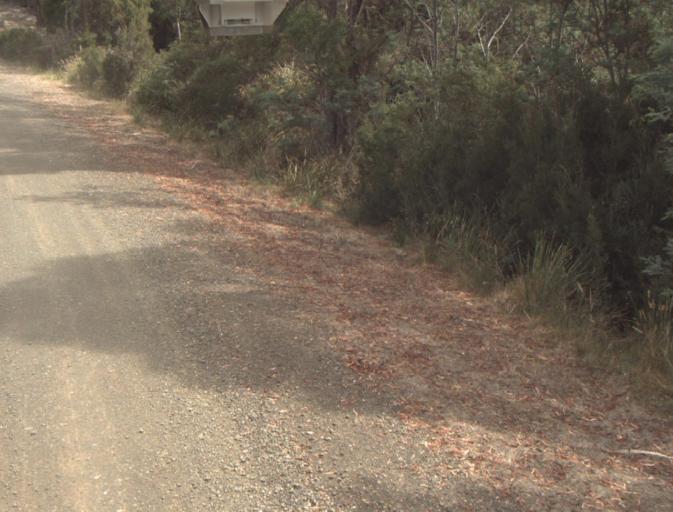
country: AU
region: Tasmania
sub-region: Launceston
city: Mayfield
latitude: -41.2748
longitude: 147.0492
